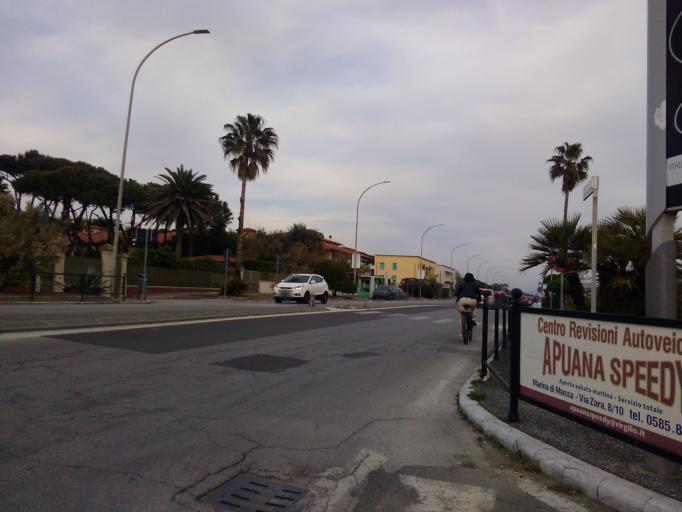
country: IT
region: Tuscany
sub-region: Provincia di Massa-Carrara
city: Massa
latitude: 44.0024
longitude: 10.1078
